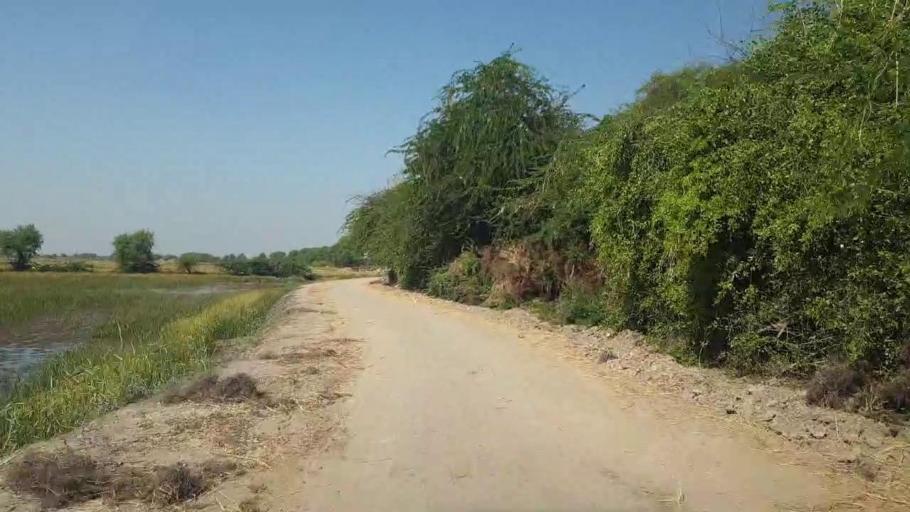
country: PK
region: Sindh
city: Talhar
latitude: 24.8039
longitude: 68.8095
